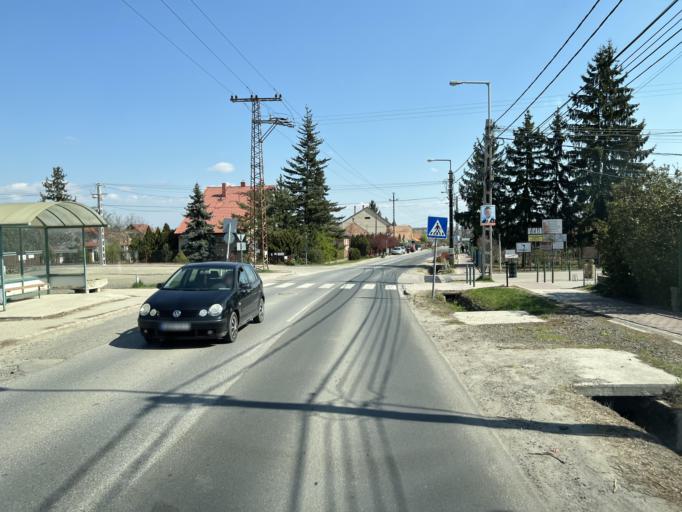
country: HU
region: Pest
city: Orbottyan
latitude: 47.6835
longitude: 19.2768
